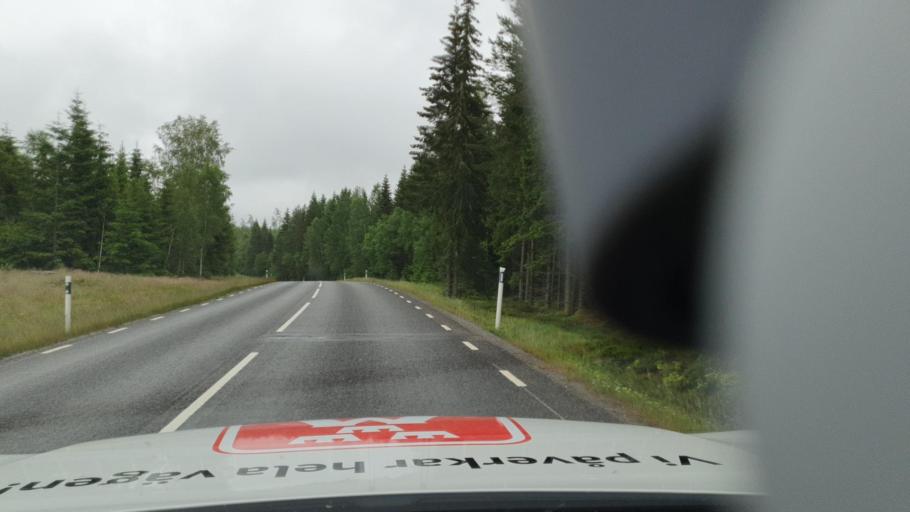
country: SE
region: OErebro
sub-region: Degerfors Kommun
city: Degerfors
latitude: 59.2218
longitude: 14.3474
